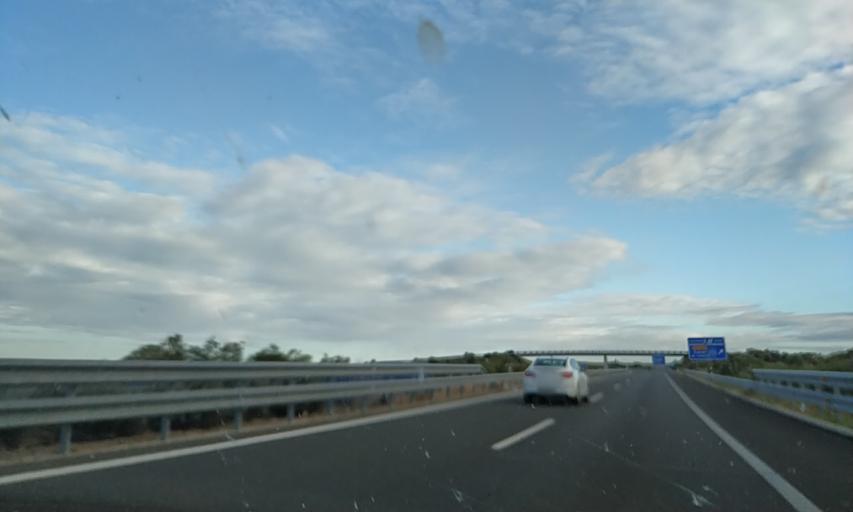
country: ES
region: Extremadura
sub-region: Provincia de Caceres
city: Casar de Caceres
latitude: 39.5703
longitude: -6.4016
